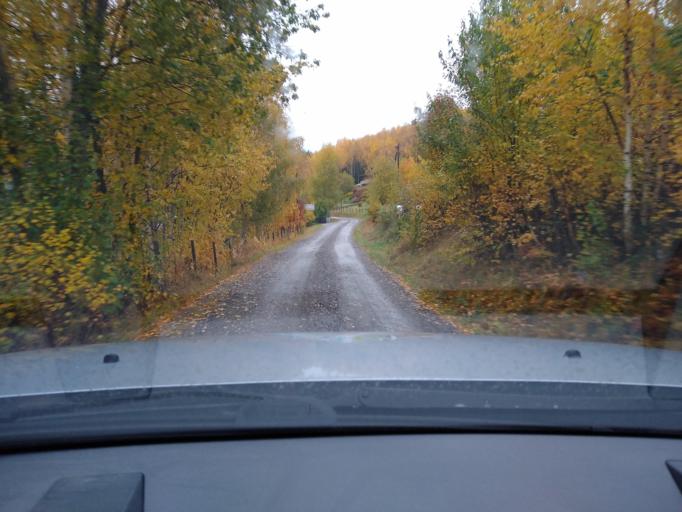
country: NO
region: Oppland
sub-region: Ringebu
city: Ringebu
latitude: 61.5485
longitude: 10.1496
